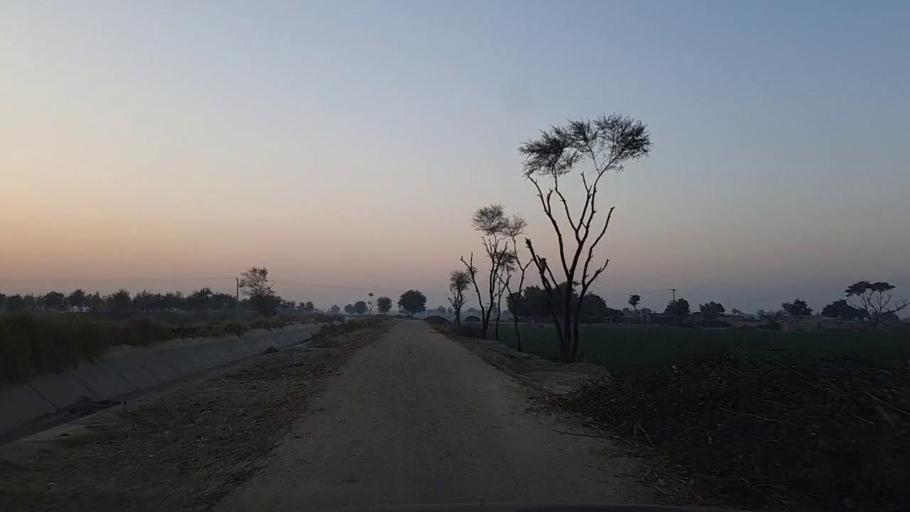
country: PK
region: Sindh
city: Daur
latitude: 26.4763
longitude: 68.4988
